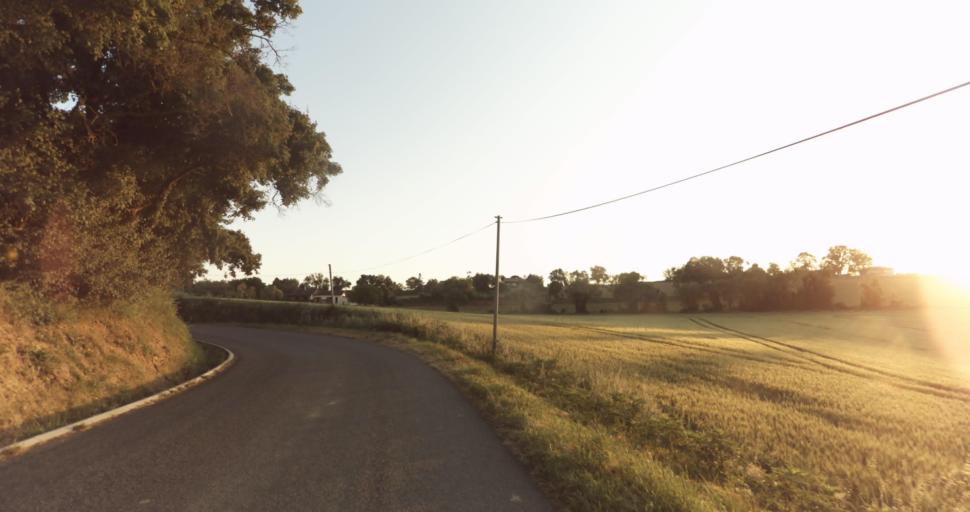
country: FR
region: Midi-Pyrenees
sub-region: Departement du Gers
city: Pujaudran
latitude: 43.6461
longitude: 1.1079
